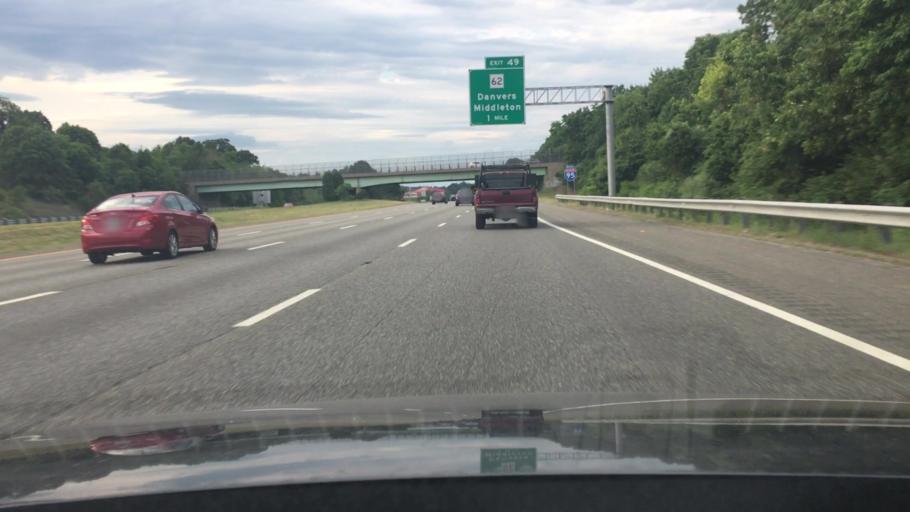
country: US
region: Massachusetts
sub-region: Essex County
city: Danvers
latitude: 42.5664
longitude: -70.9709
